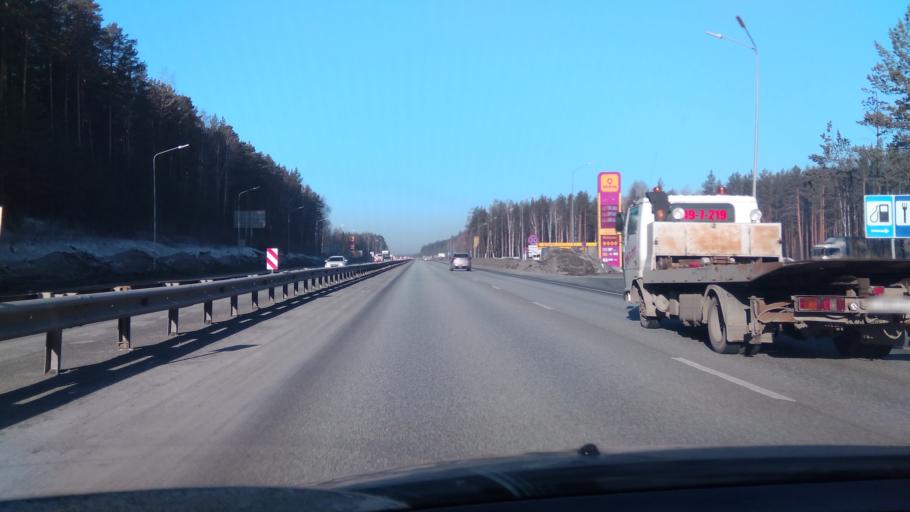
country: RU
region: Sverdlovsk
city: Severka
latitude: 56.8386
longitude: 60.2715
